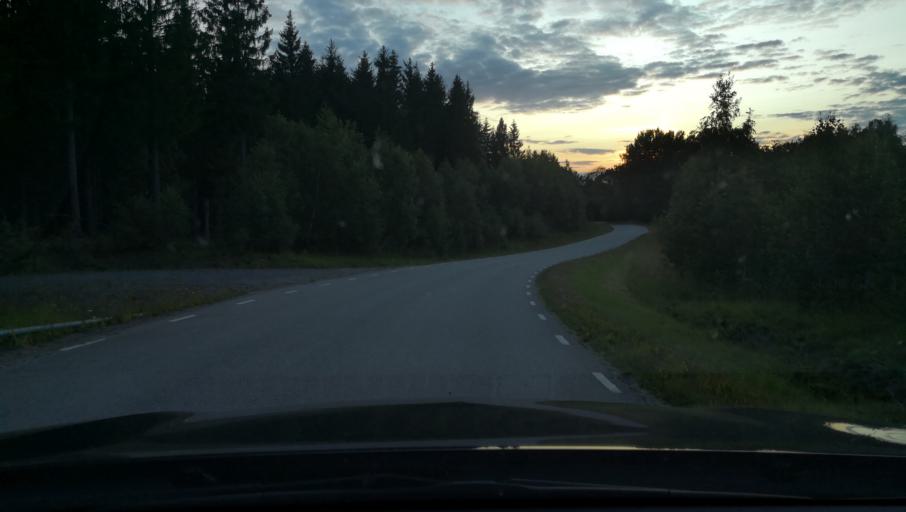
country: SE
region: Uppsala
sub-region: Osthammars Kommun
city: Bjorklinge
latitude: 60.0543
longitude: 17.6145
